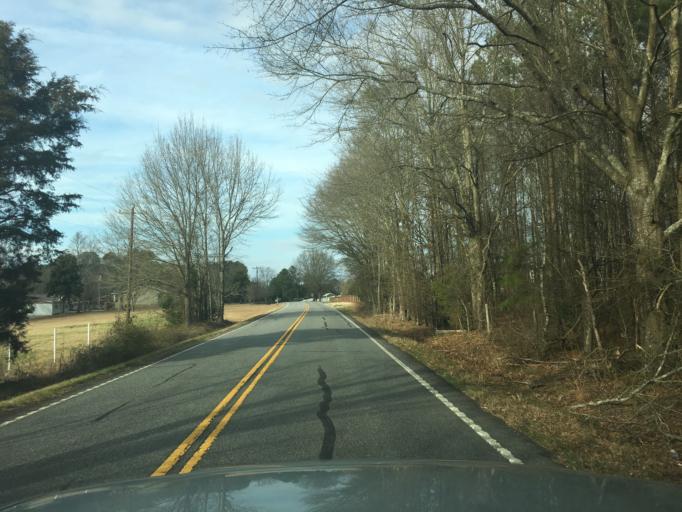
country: US
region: South Carolina
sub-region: Abbeville County
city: Lake Secession
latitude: 34.3640
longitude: -82.5202
